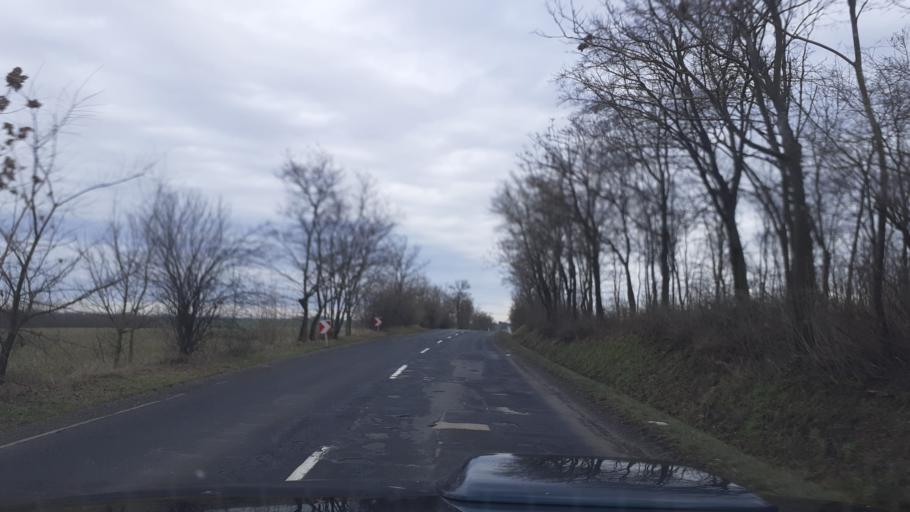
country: HU
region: Fejer
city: Mezofalva
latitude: 46.9703
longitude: 18.7245
